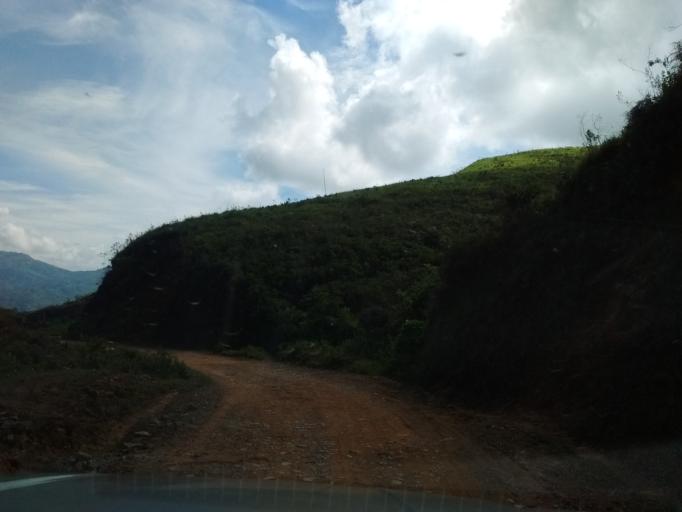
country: CO
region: Cauca
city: Morales
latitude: 2.6893
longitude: -76.7474
